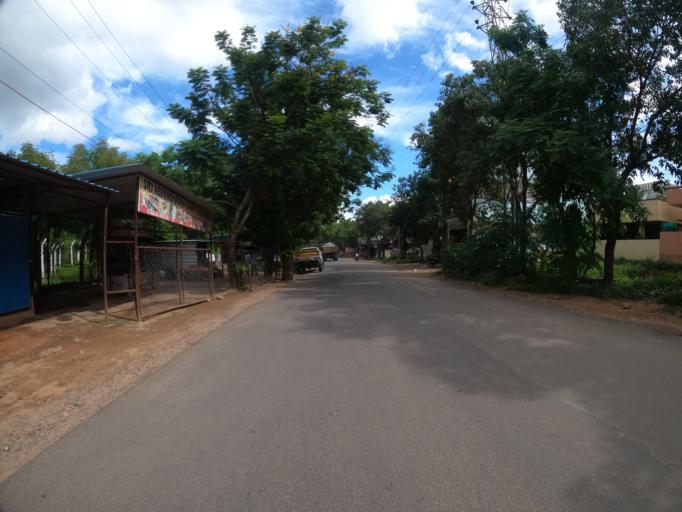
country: IN
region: Telangana
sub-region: Hyderabad
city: Hyderabad
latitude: 17.3564
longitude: 78.3884
